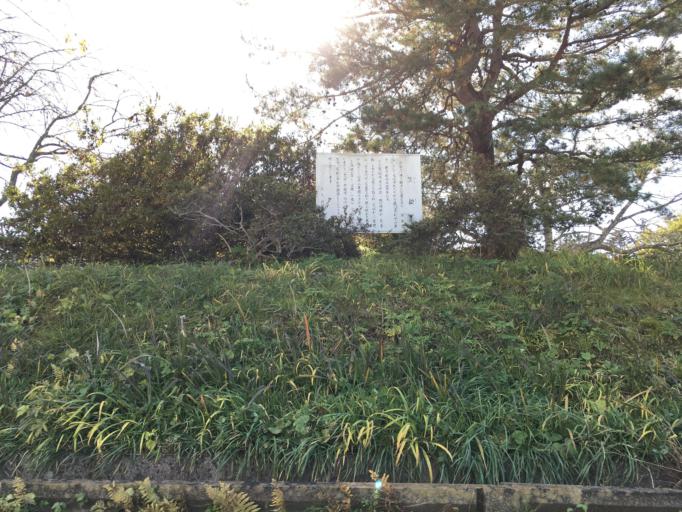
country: JP
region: Iwate
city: Ichinoseki
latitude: 38.9528
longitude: 141.3823
